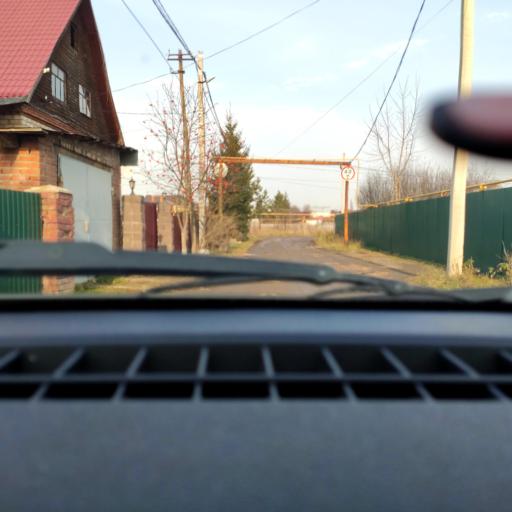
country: RU
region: Bashkortostan
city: Iglino
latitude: 54.8216
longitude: 56.1844
